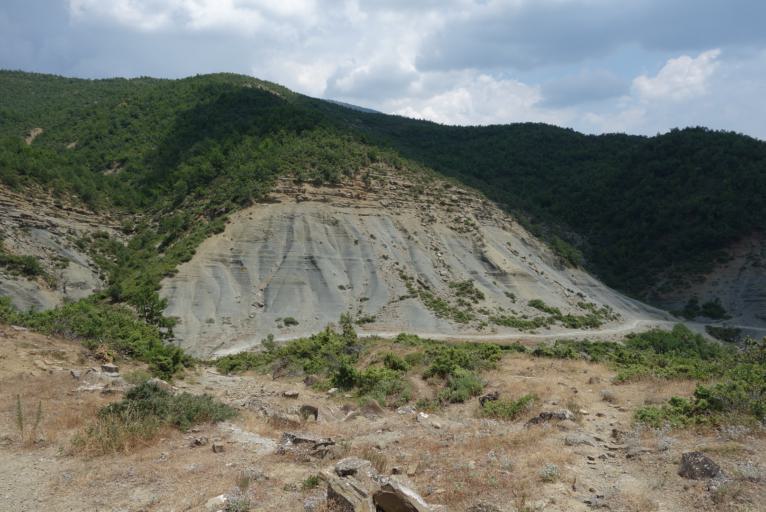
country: AL
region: Berat
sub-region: Rrethi i Skraparit
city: Cepan
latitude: 40.4004
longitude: 20.3429
